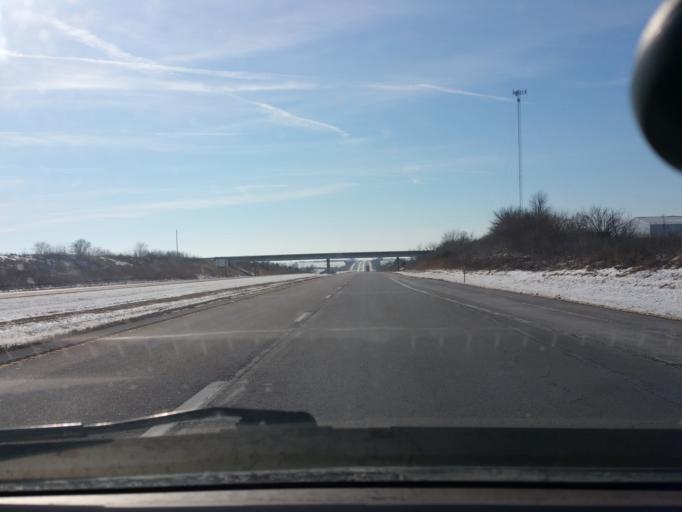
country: US
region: Iowa
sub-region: Decatur County
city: Lamoni
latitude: 40.5175
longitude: -93.9627
